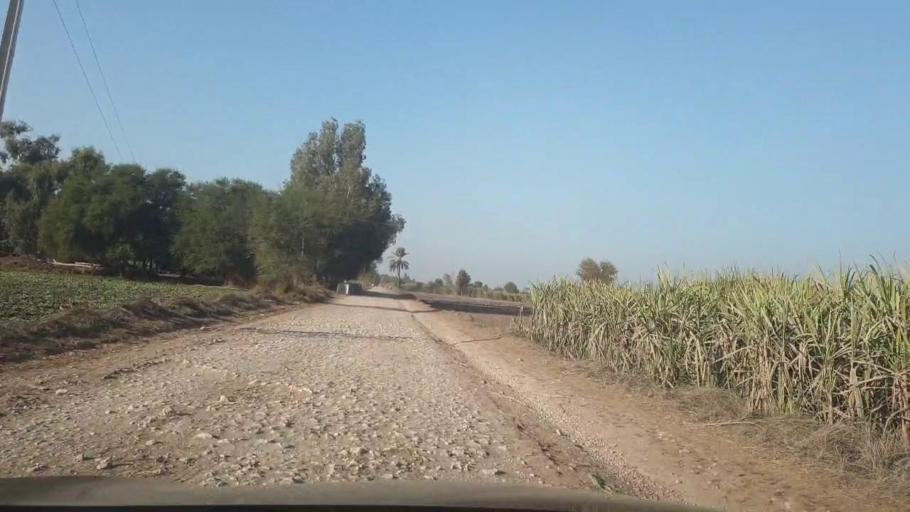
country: PK
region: Sindh
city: Ubauro
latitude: 28.1504
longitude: 69.6091
